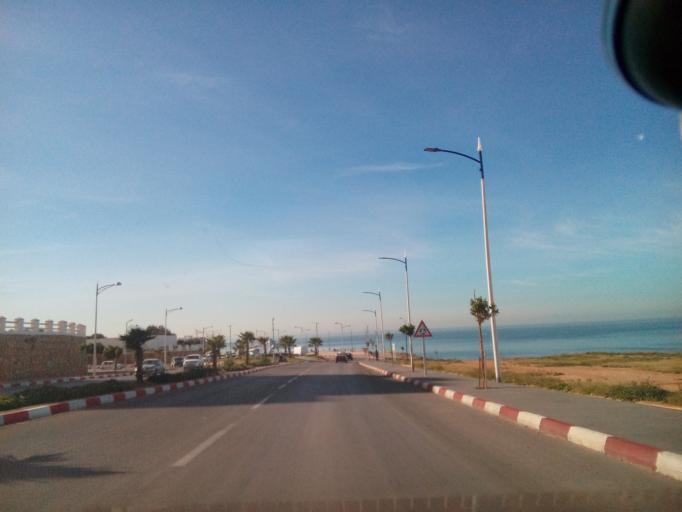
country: DZ
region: Mostaganem
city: Mostaganem
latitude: 35.9445
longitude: 0.0863
